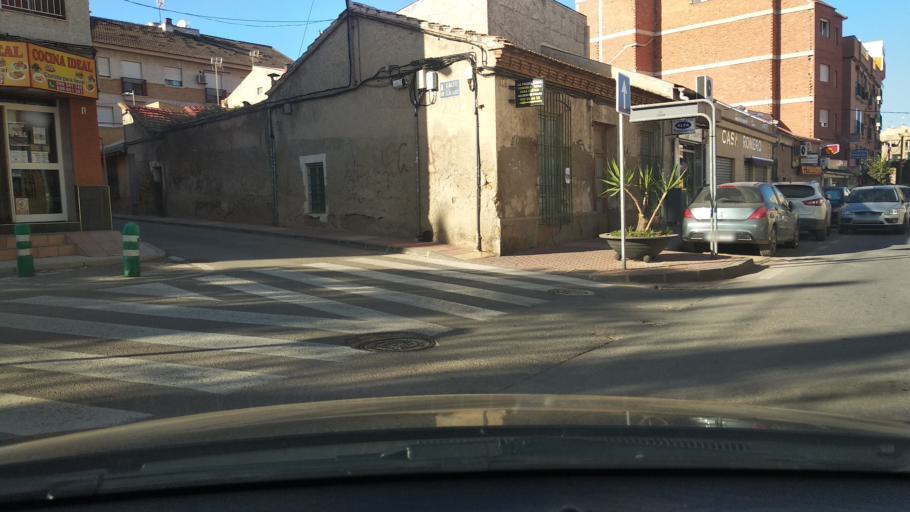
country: ES
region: Murcia
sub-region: Murcia
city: Murcia
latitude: 37.9439
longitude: -1.1286
